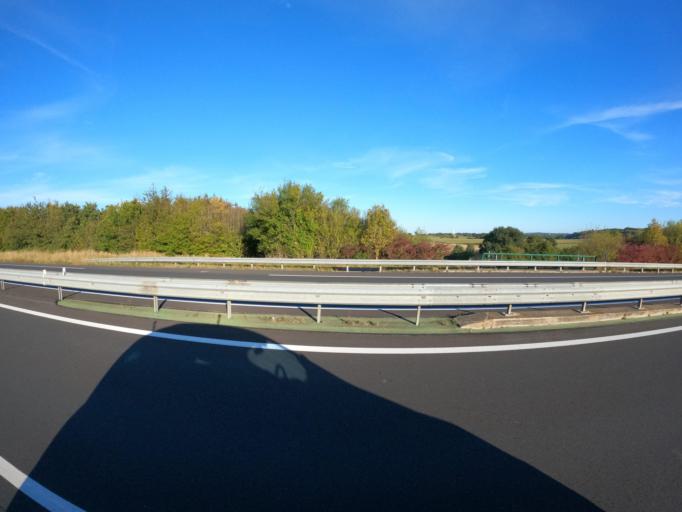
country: FR
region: Pays de la Loire
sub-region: Departement de la Vendee
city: Saint-Laurent-sur-Sevre
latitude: 46.9737
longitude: -0.9177
